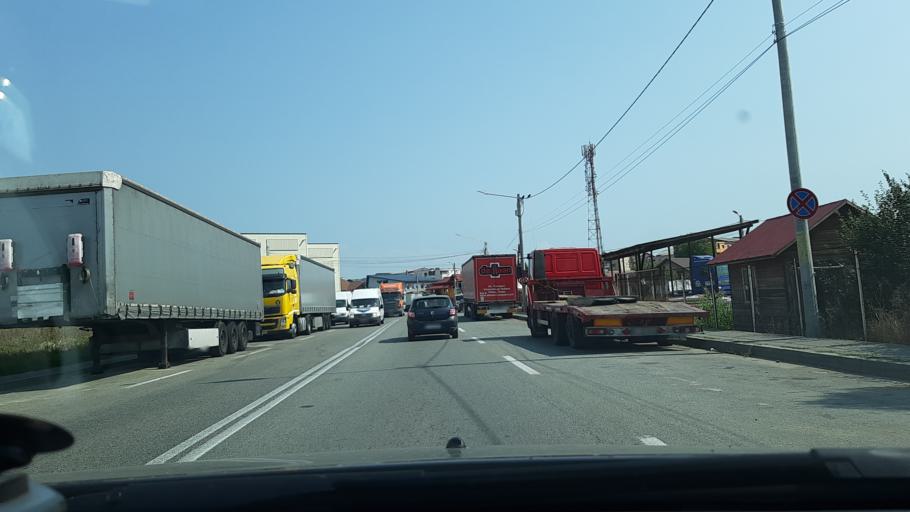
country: RO
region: Gorj
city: Targu Jiu
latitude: 45.0220
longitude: 23.2642
